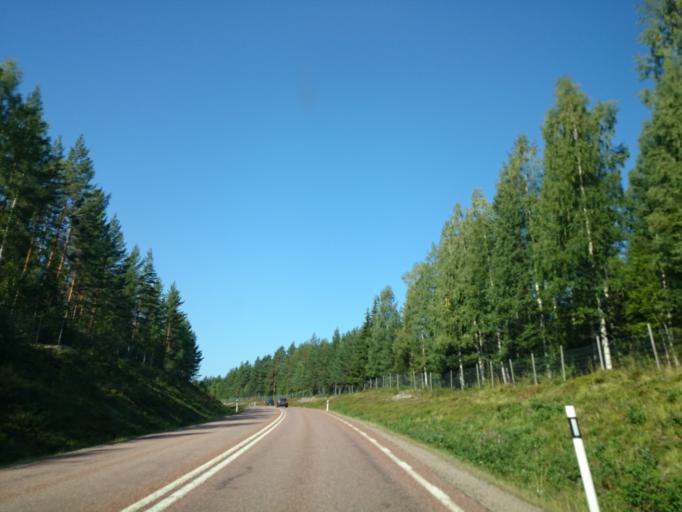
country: SE
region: Gaevleborg
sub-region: Hudiksvalls Kommun
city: Delsbo
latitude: 61.7645
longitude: 16.7612
